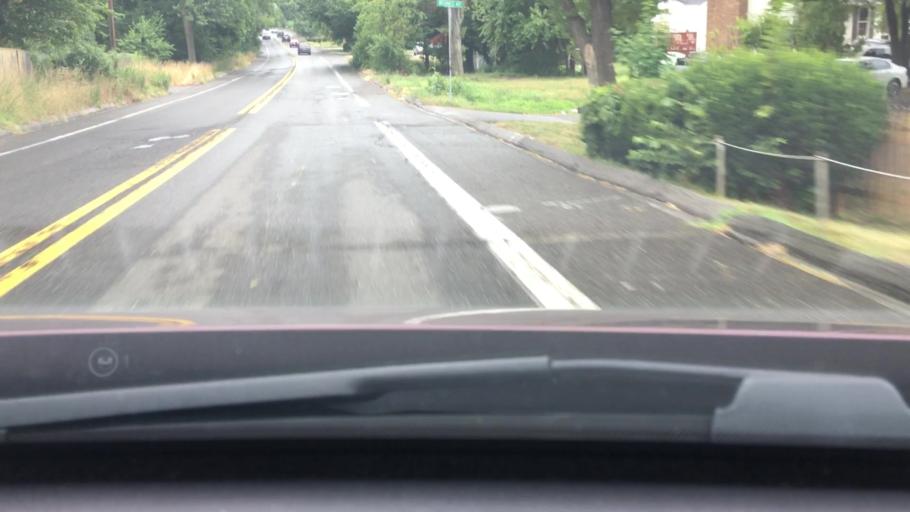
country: US
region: Maryland
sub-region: Prince George's County
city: Beltsville
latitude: 39.0410
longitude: -76.9122
